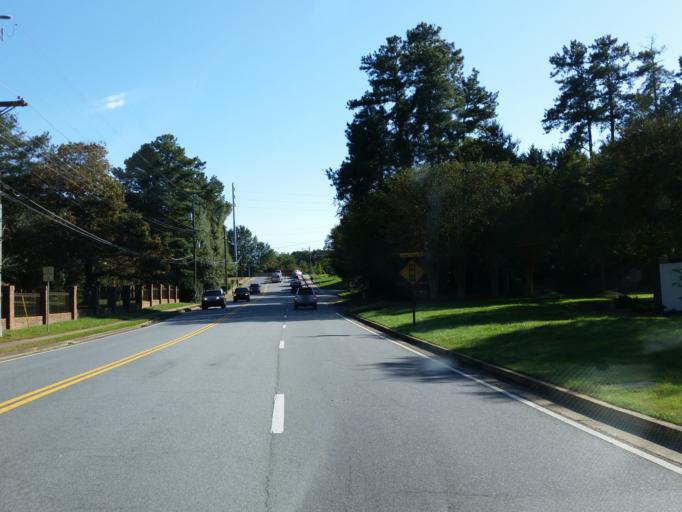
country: US
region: Georgia
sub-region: Cherokee County
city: Woodstock
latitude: 34.0273
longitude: -84.4810
